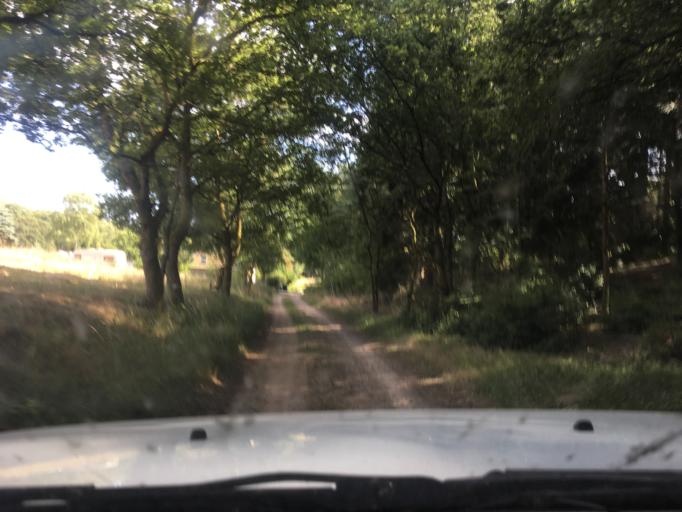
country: DK
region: Central Jutland
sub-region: Viborg Kommune
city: Viborg
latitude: 56.4341
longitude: 9.4585
